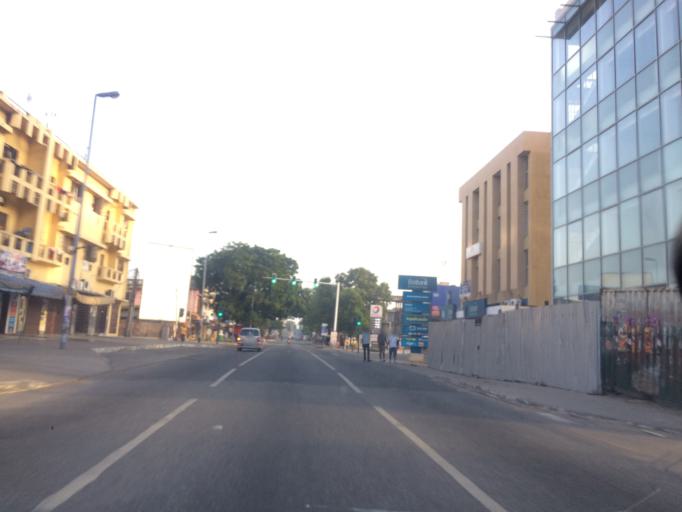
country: GH
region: Greater Accra
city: Accra
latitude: 5.5602
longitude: -0.2130
